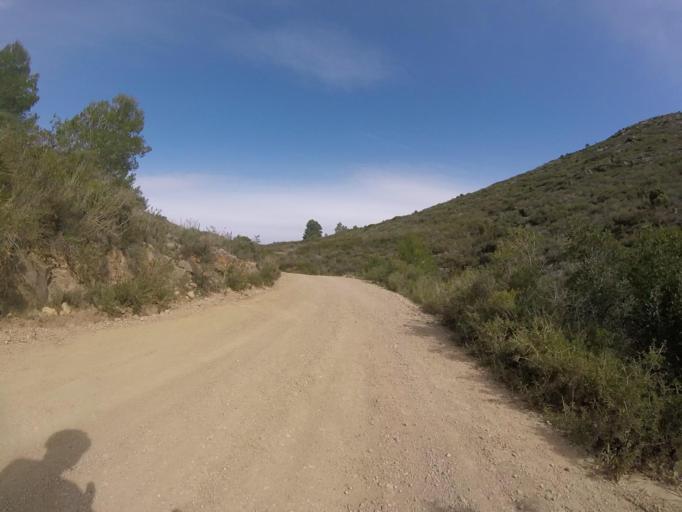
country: ES
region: Valencia
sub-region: Provincia de Castello
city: Torreblanca
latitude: 40.2011
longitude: 0.1530
